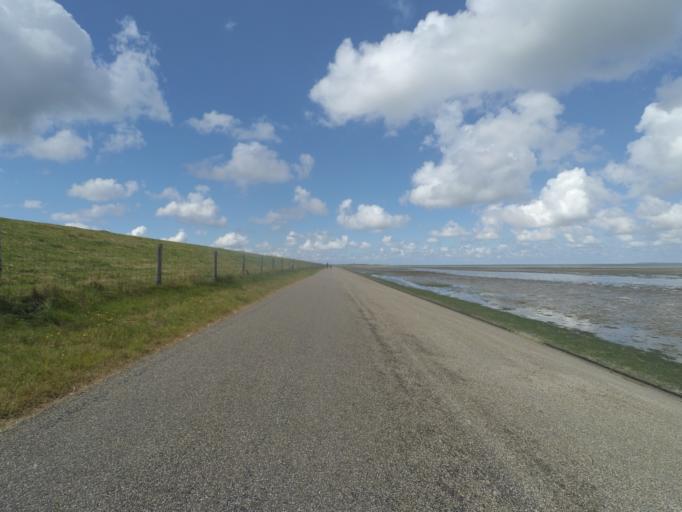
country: NL
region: North Holland
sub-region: Gemeente Texel
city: Den Burg
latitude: 53.1530
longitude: 4.8911
